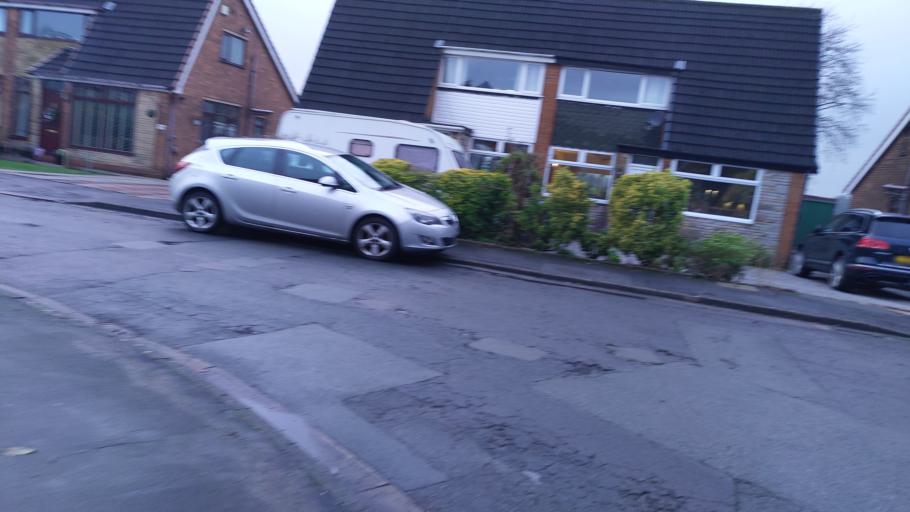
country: GB
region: England
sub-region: Lancashire
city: Euxton
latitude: 53.6749
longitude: -2.6801
